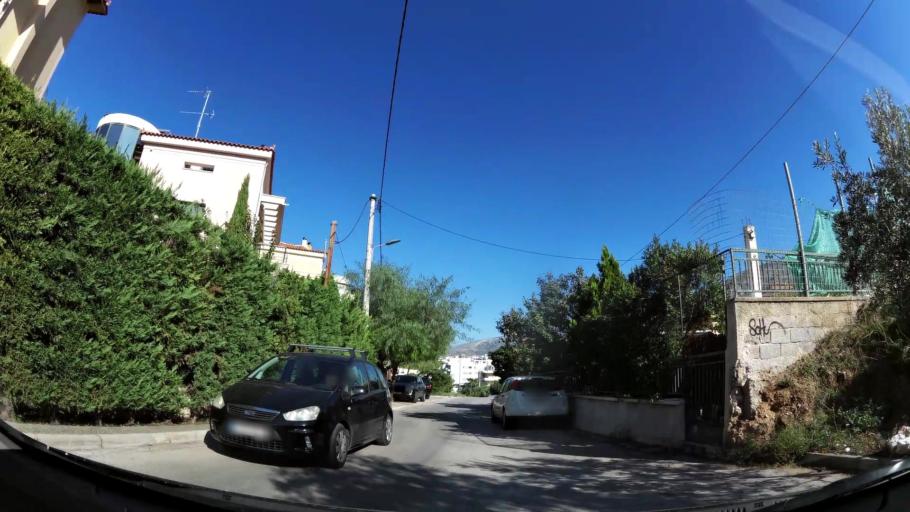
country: GR
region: Attica
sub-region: Nomarchia Athinas
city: Glyfada
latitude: 37.8658
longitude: 23.7695
